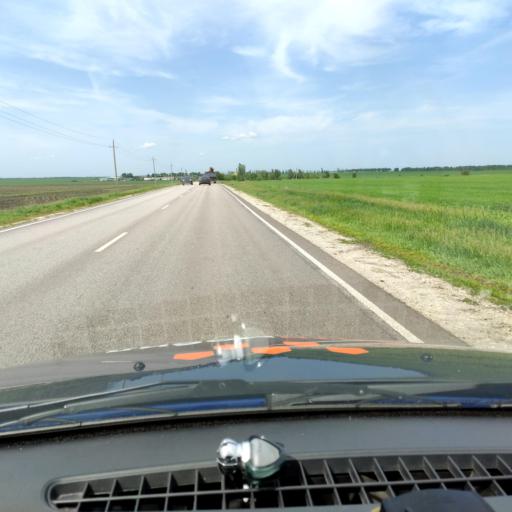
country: RU
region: Voronezj
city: Novaya Usman'
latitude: 51.5658
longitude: 39.3758
